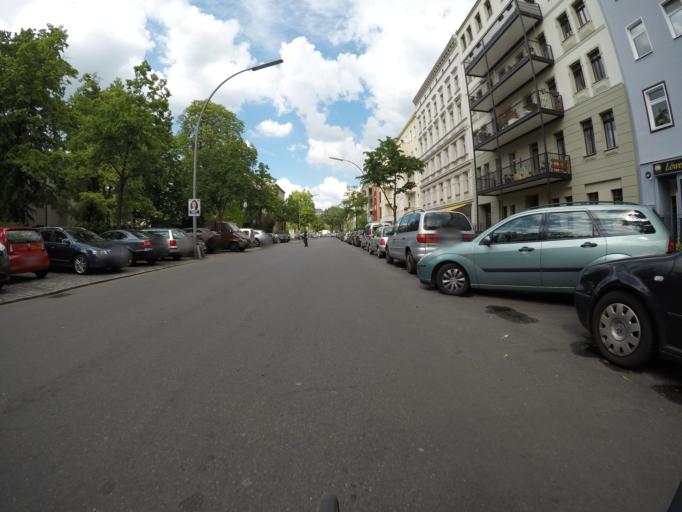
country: DE
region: Berlin
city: Wedding Bezirk
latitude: 52.5550
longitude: 13.3717
